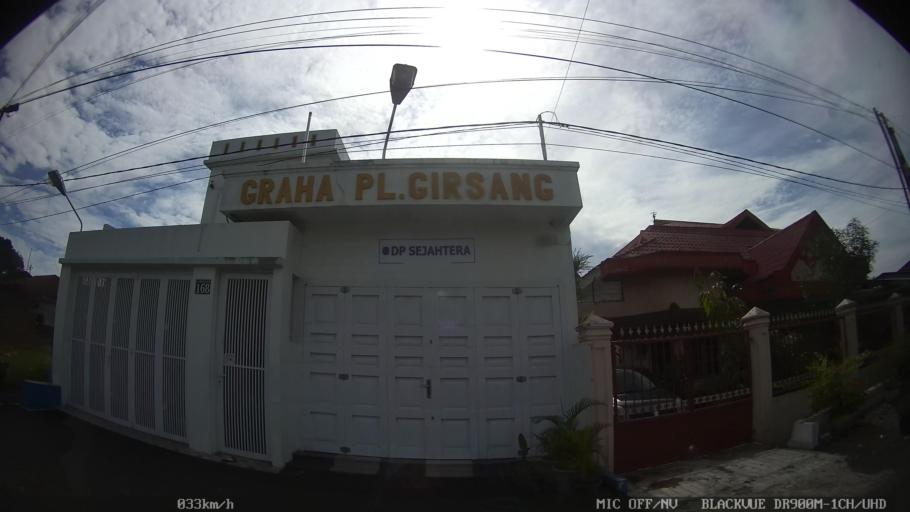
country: ID
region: North Sumatra
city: Sunggal
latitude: 3.6119
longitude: 98.6296
